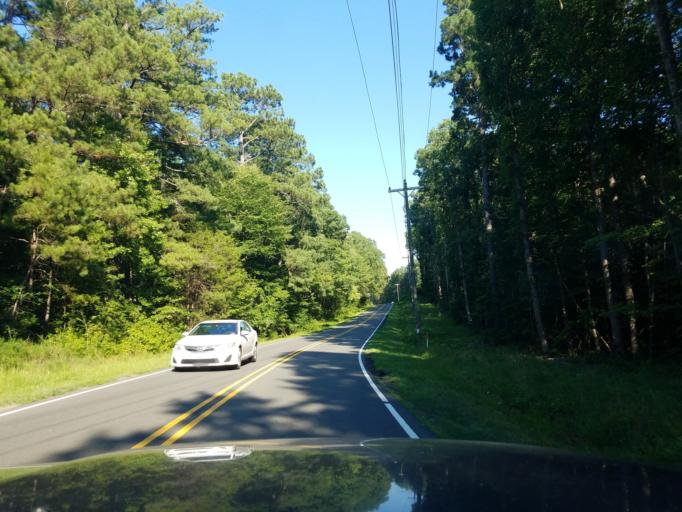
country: US
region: North Carolina
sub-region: Wake County
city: Green Level
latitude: 35.8762
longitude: -78.9396
